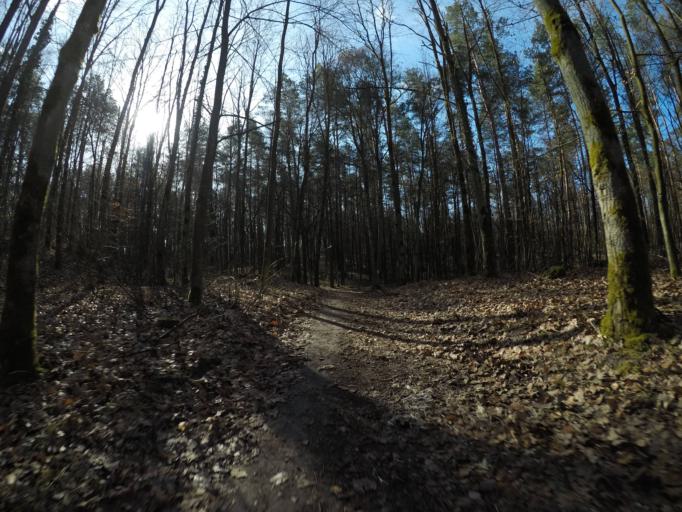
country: PL
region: Kujawsko-Pomorskie
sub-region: Powiat brodnicki
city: Gorzno
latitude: 53.1899
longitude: 19.6591
